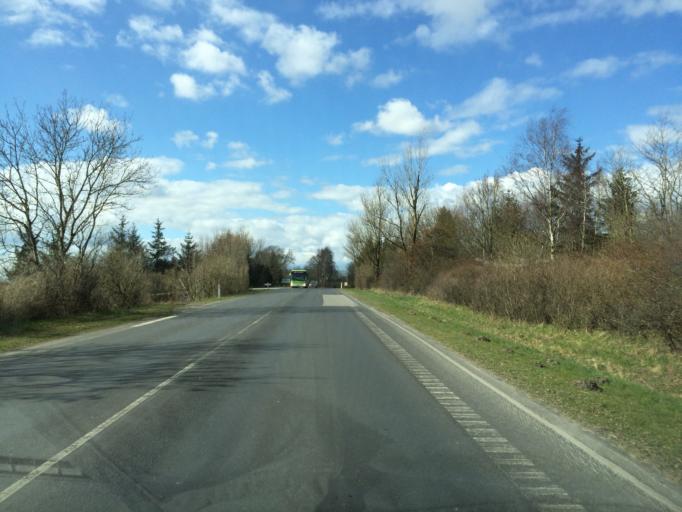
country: DK
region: South Denmark
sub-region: Assens Kommune
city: Arup
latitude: 55.4260
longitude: 10.0226
